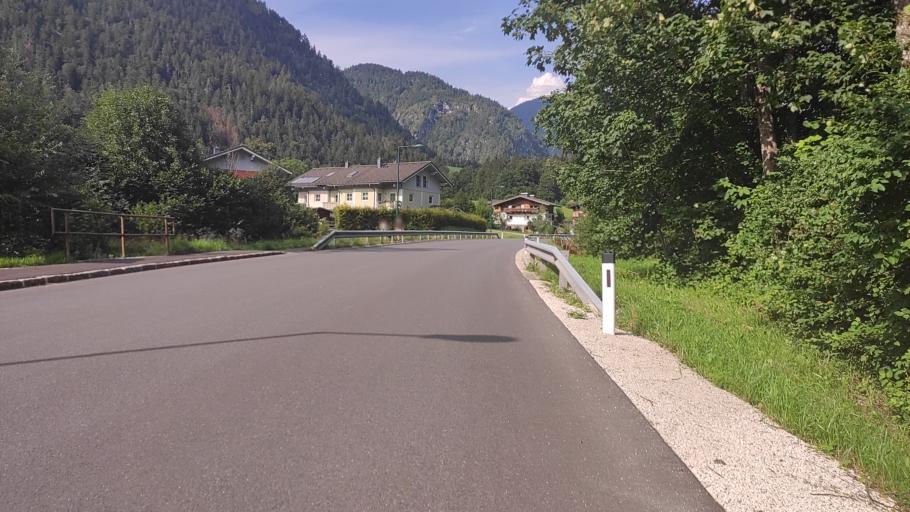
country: AT
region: Salzburg
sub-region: Politischer Bezirk Zell am See
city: Unken
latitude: 47.6603
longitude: 12.7411
